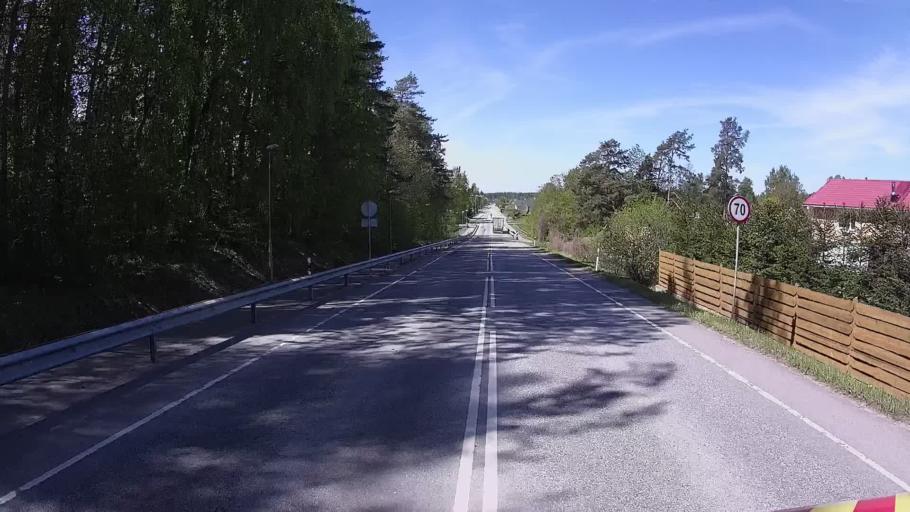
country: EE
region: Vorumaa
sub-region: Voru linn
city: Voru
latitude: 57.8127
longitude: 27.0475
